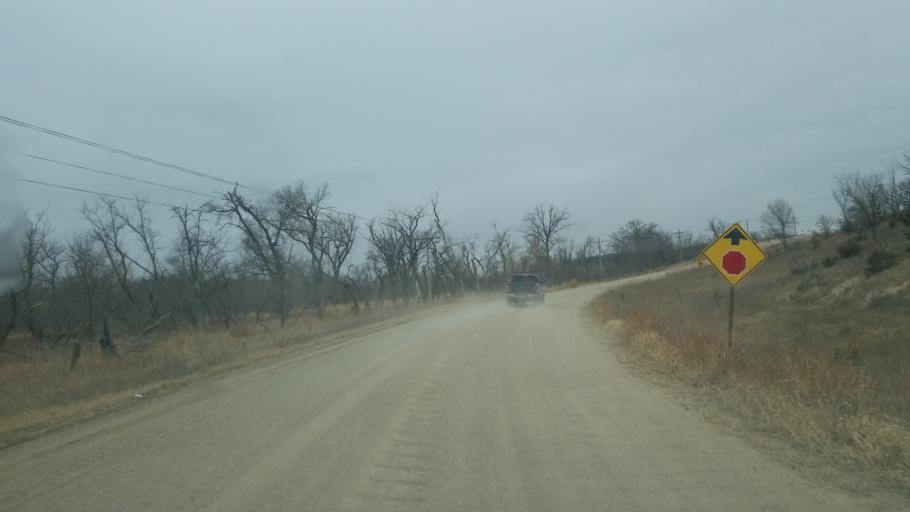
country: US
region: South Dakota
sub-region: Bon Homme County
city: Springfield
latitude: 42.7406
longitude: -97.9281
